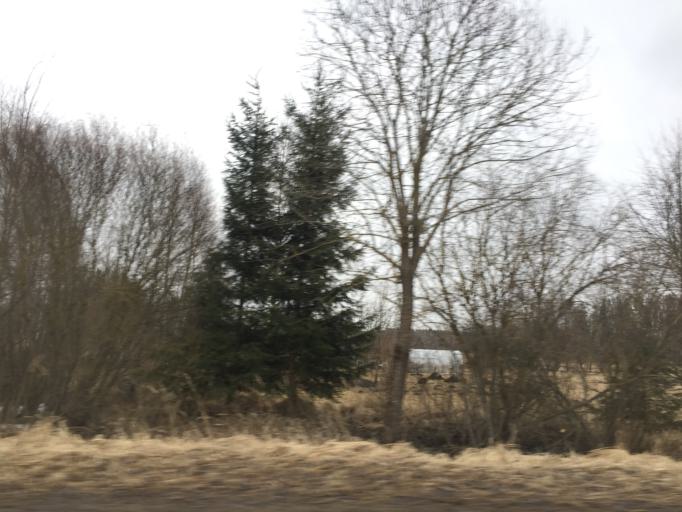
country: LV
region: Lielvarde
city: Lielvarde
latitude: 56.7365
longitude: 24.8214
